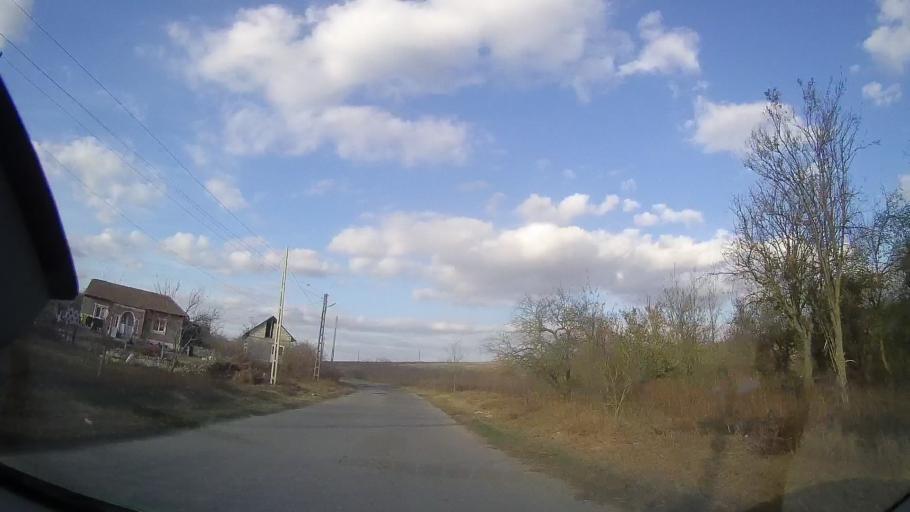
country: RO
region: Constanta
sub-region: Comuna Cerchezu
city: Cerchezu
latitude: 43.8265
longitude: 28.0977
